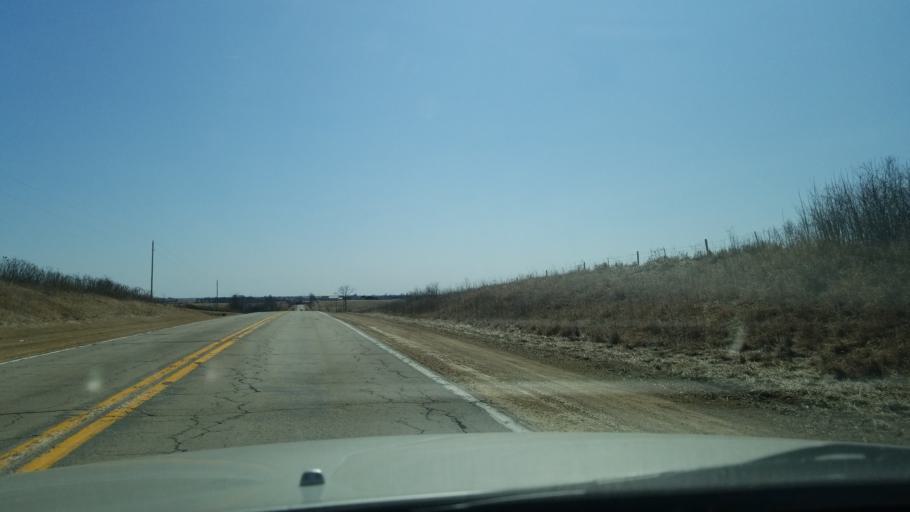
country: US
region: Wisconsin
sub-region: Iowa County
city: Mineral Point
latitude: 42.8970
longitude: -90.2260
